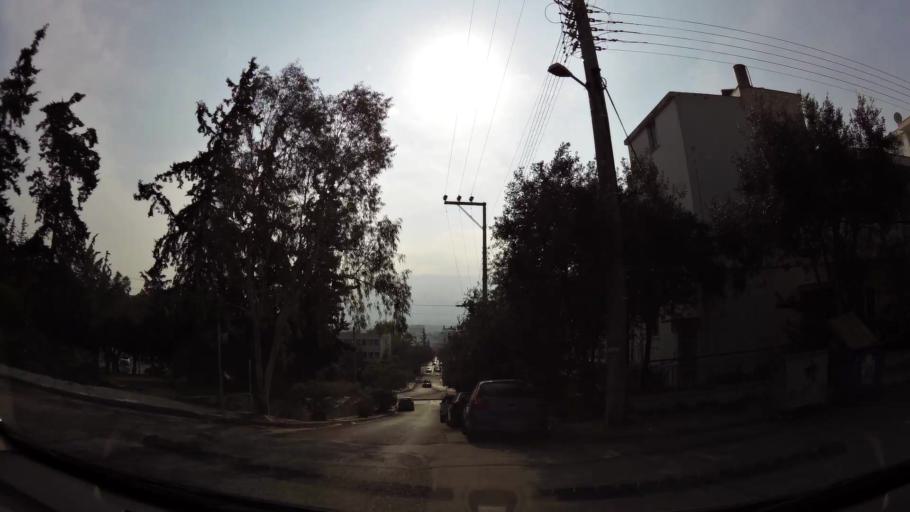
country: GR
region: Attica
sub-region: Nomarchia Athinas
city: Psychiko
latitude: 38.0016
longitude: 23.7650
